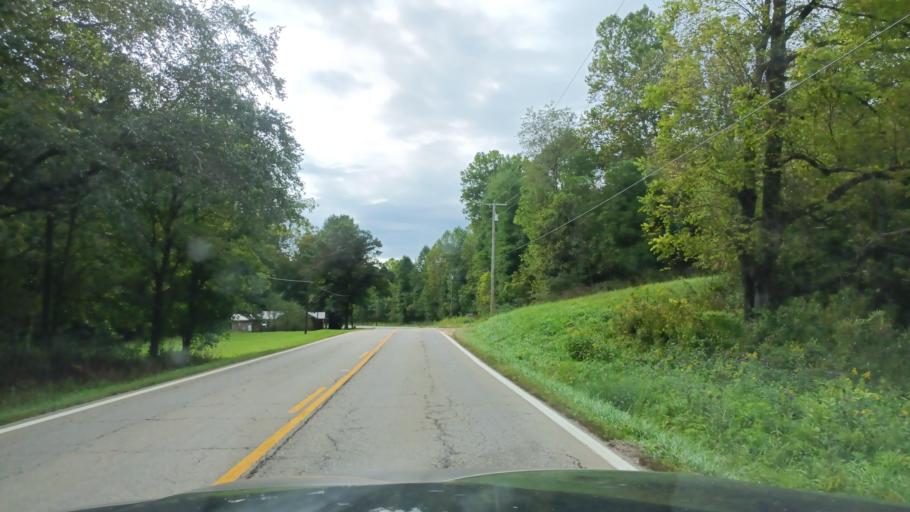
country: US
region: Ohio
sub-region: Vinton County
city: McArthur
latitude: 39.2699
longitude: -82.5789
